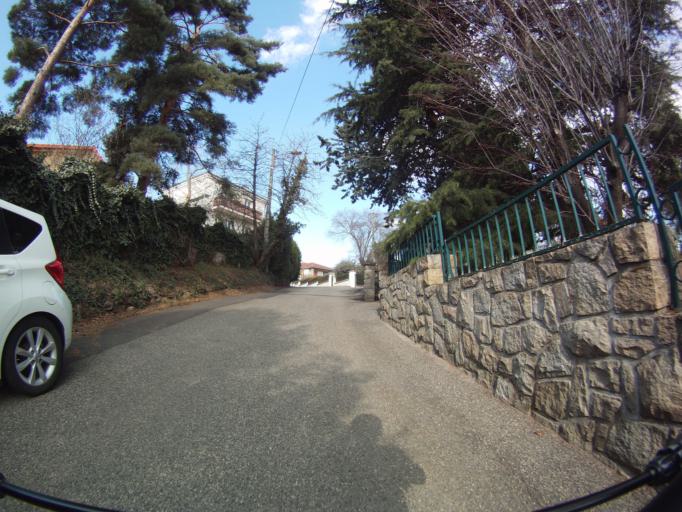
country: FR
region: Auvergne
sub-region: Departement du Puy-de-Dome
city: Ceyrat
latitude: 45.7365
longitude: 3.0628
